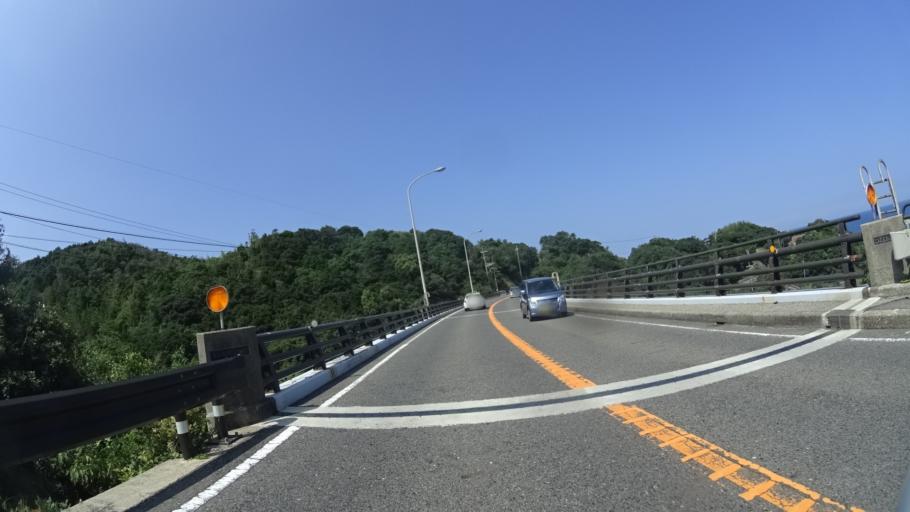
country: JP
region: Shimane
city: Masuda
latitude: 34.6727
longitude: 131.7246
